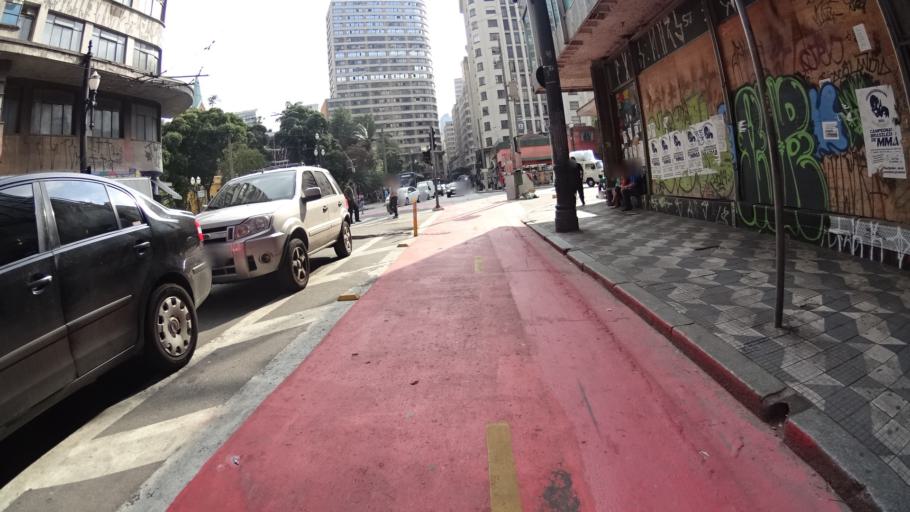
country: BR
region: Sao Paulo
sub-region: Sao Paulo
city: Sao Paulo
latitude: -23.5420
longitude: -46.6373
